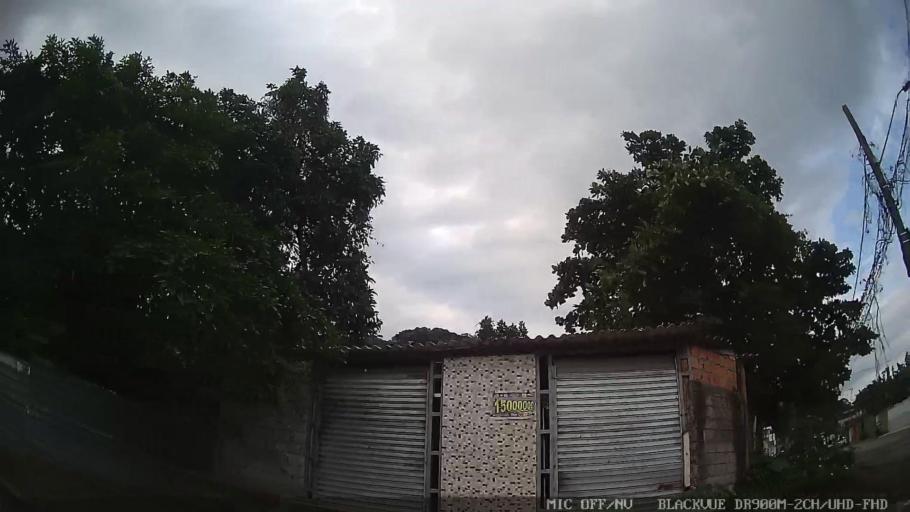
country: BR
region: Sao Paulo
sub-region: Guaruja
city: Guaruja
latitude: -23.9821
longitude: -46.2441
